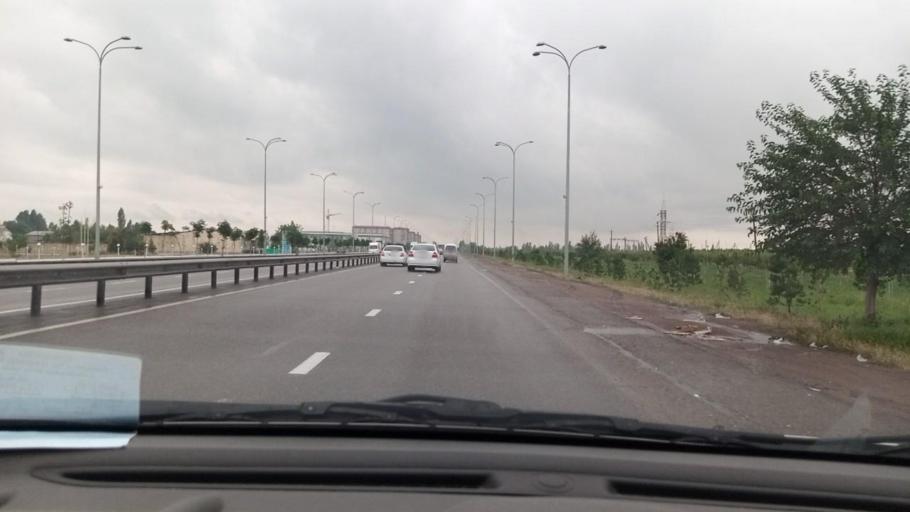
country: UZ
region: Toshkent
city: Ohangaron
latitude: 40.9110
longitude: 69.6194
